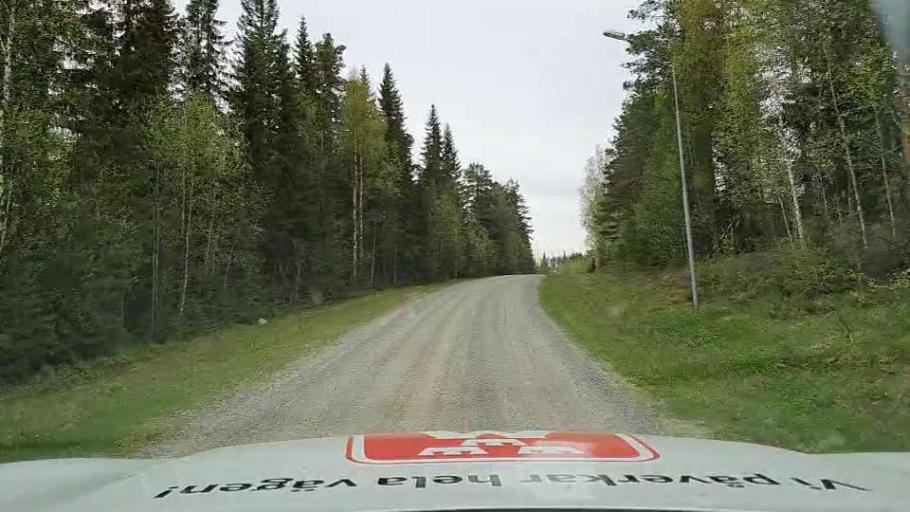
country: SE
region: Jaemtland
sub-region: Bergs Kommun
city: Hoverberg
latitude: 62.5664
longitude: 14.6718
